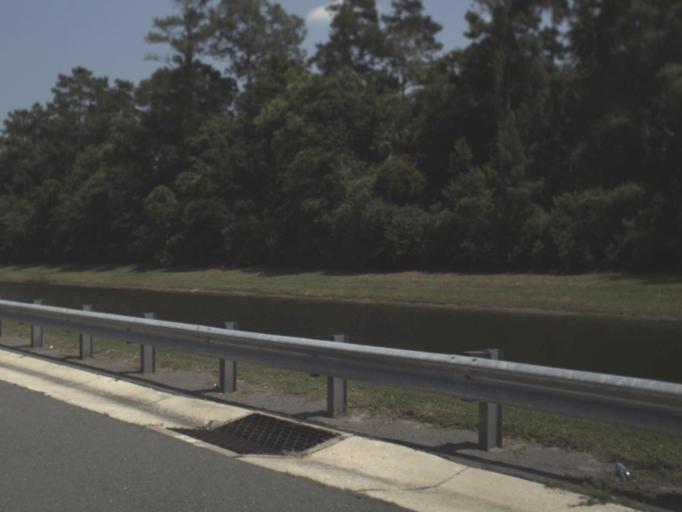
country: US
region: Florida
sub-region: Duval County
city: Atlantic Beach
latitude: 30.3590
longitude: -81.4533
